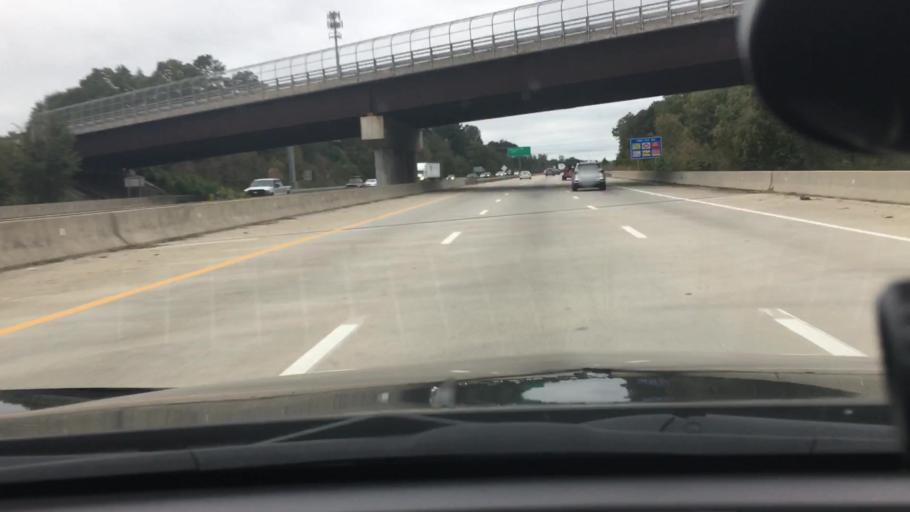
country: US
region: North Carolina
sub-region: Wake County
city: Knightdale
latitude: 35.7740
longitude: -78.5482
